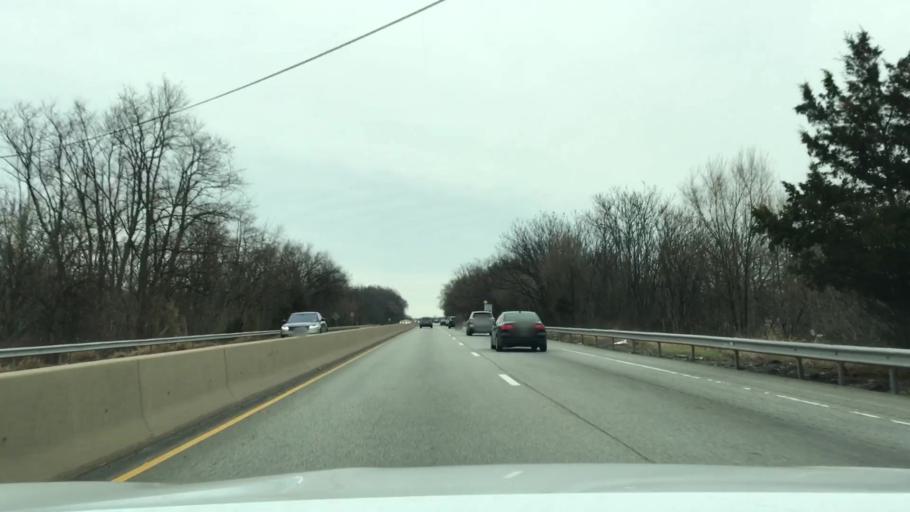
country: US
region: Pennsylvania
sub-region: Montgomery County
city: Pottstown
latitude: 40.2563
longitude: -75.6575
